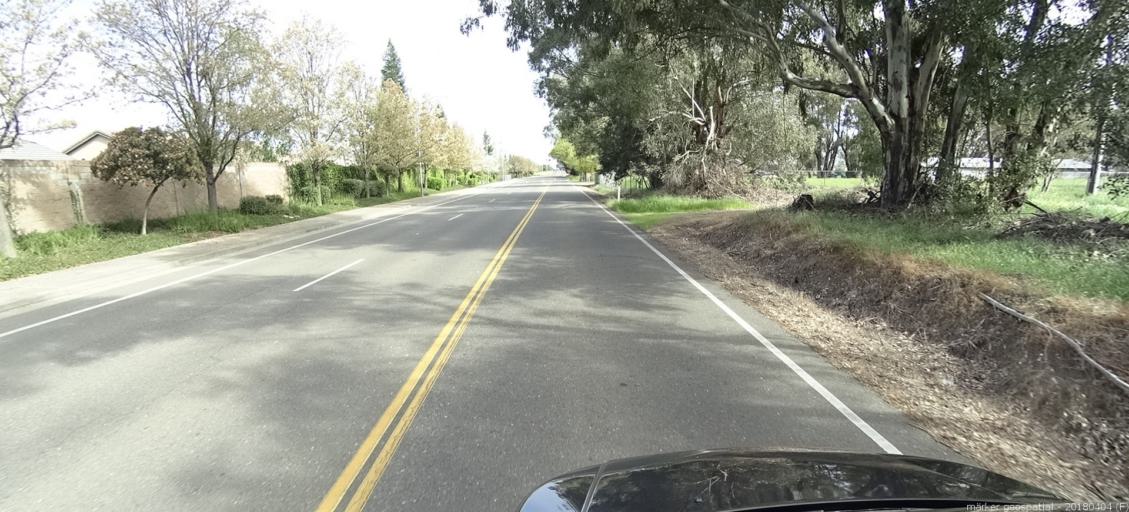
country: US
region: California
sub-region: Sacramento County
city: Galt
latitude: 38.2810
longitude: -121.2826
